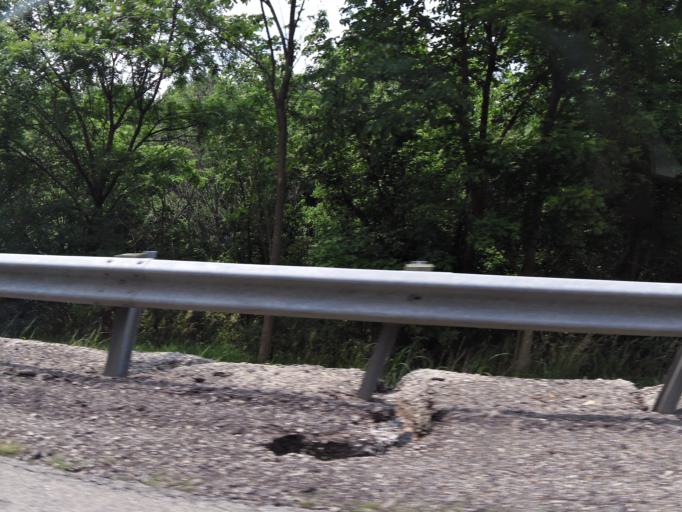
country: US
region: Kentucky
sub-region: Henry County
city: New Castle
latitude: 38.4758
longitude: -85.2719
